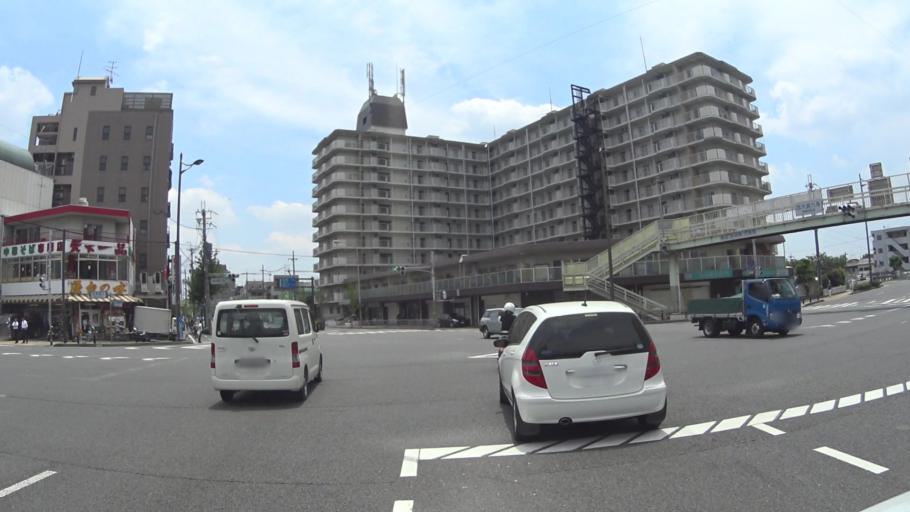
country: JP
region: Kyoto
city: Muko
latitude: 34.9786
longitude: 135.7329
